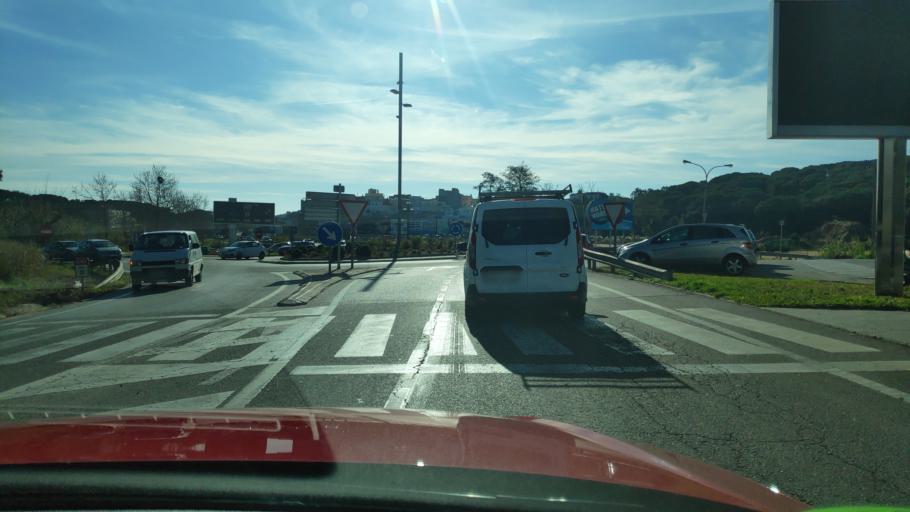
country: ES
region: Catalonia
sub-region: Provincia de Girona
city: Lloret de Mar
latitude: 41.7095
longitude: 2.8322
